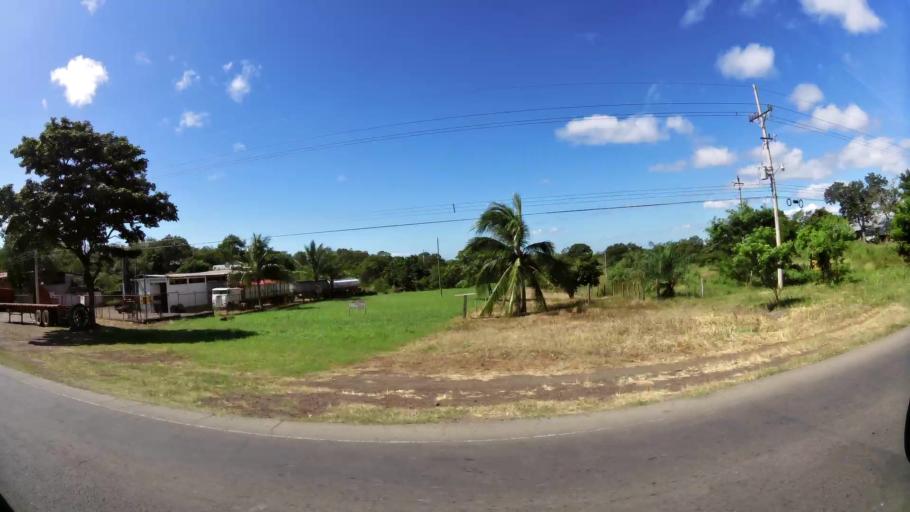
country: CR
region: Guanacaste
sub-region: Canton de Canas
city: Canas
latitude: 10.4122
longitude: -85.0853
